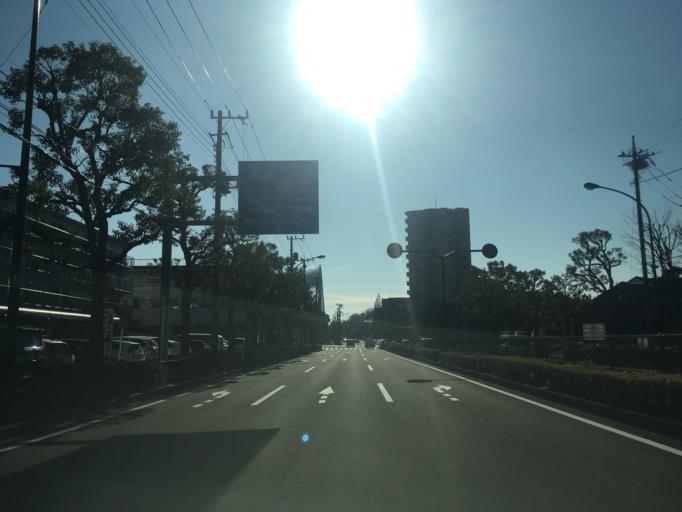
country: JP
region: Tokyo
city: Hino
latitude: 35.6096
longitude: 139.4258
